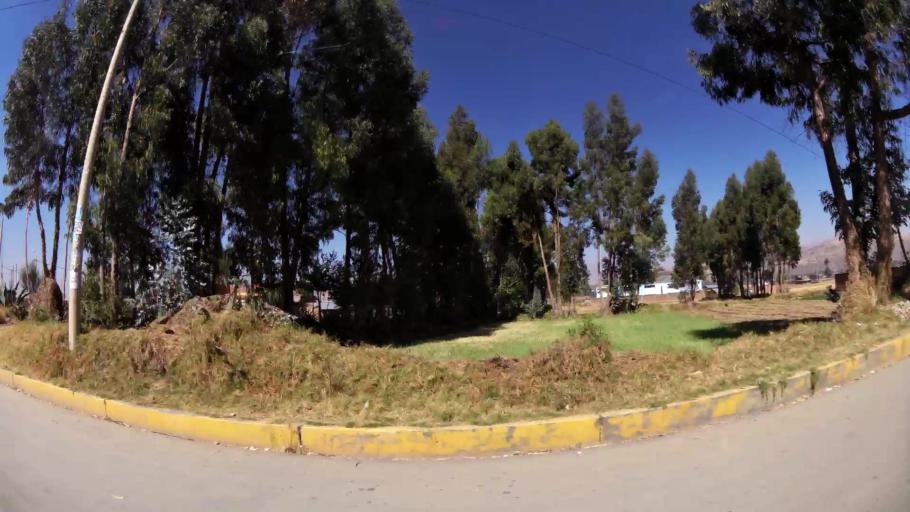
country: PE
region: Junin
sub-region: Provincia de Huancayo
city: San Jeronimo
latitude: -11.9440
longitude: -75.2895
